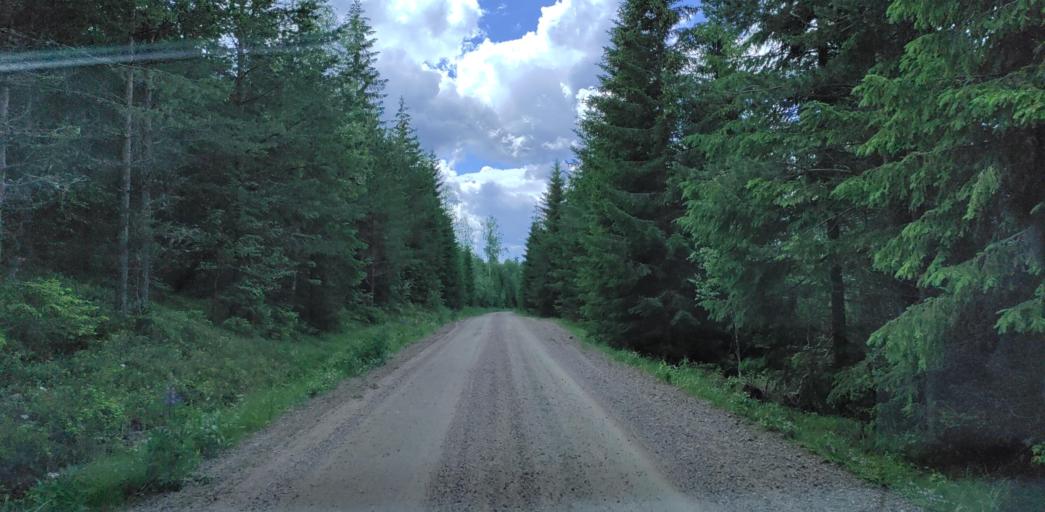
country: SE
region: Vaermland
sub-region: Hagfors Kommun
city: Ekshaerad
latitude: 60.0933
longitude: 13.3439
